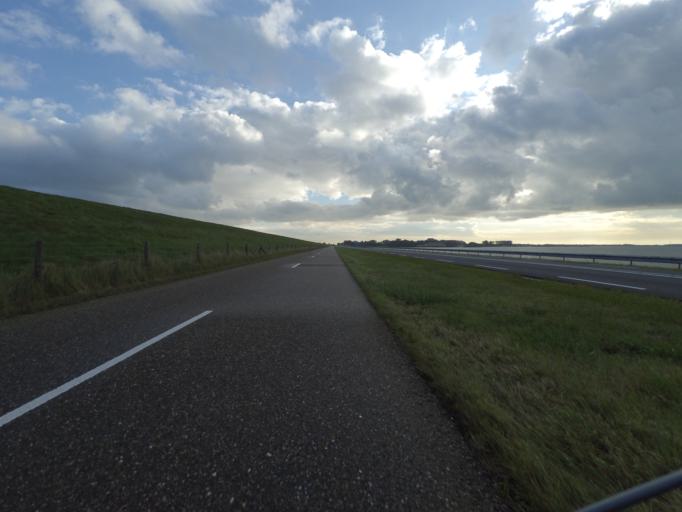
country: NL
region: North Holland
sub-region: Gemeente Hollands Kroon
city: Den Oever
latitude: 52.8906
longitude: 4.8960
